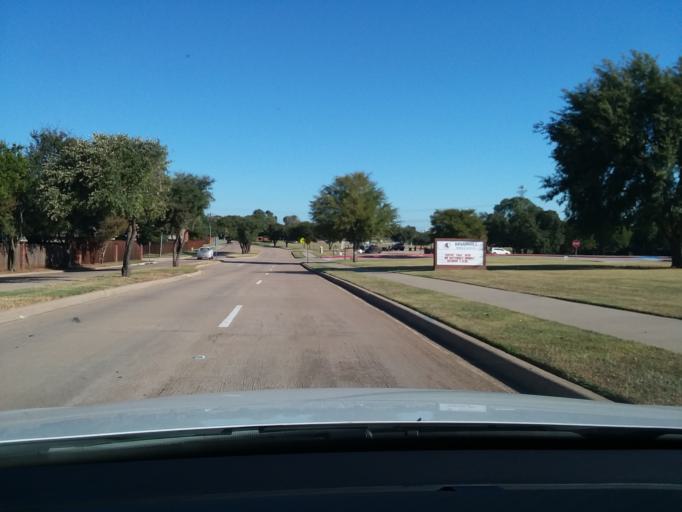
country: US
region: Texas
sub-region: Denton County
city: Highland Village
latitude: 33.0760
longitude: -97.0674
